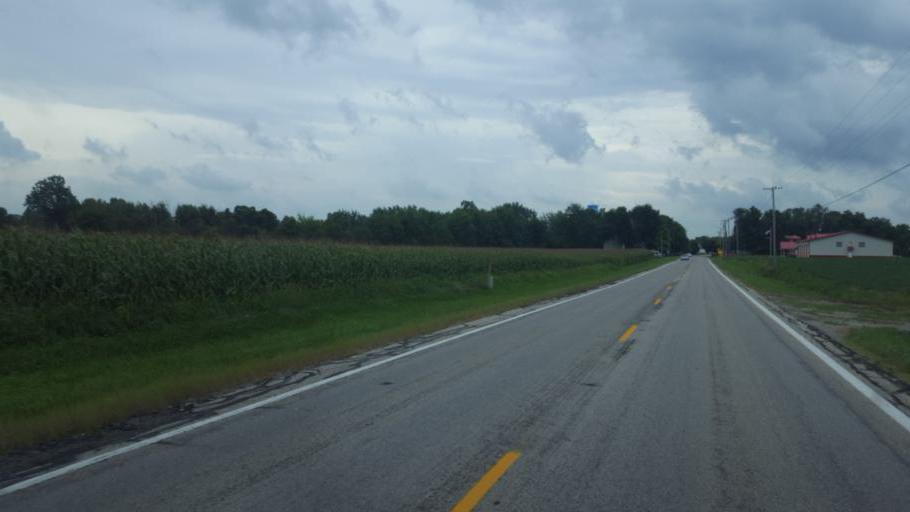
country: US
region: Ohio
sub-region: Delaware County
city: Ashley
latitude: 40.4155
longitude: -82.9538
